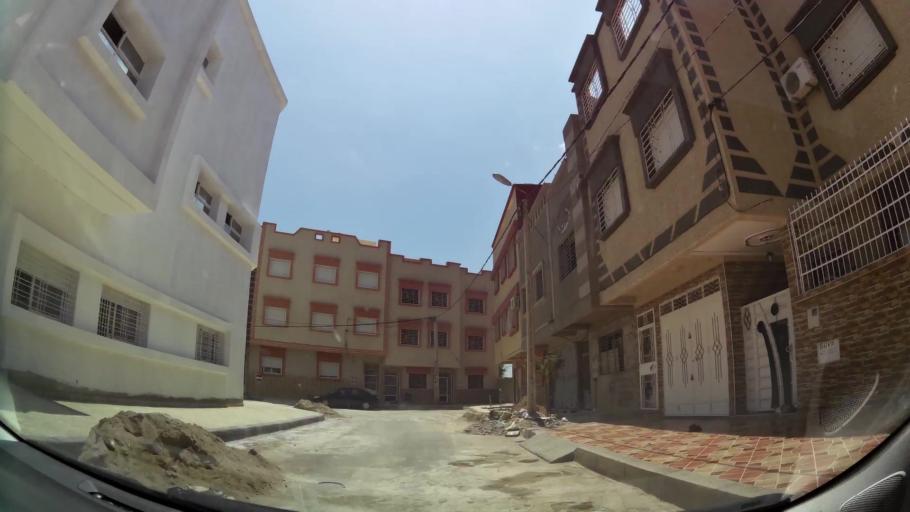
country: MA
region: Oriental
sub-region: Oujda-Angad
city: Oujda
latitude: 34.6950
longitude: -1.8935
